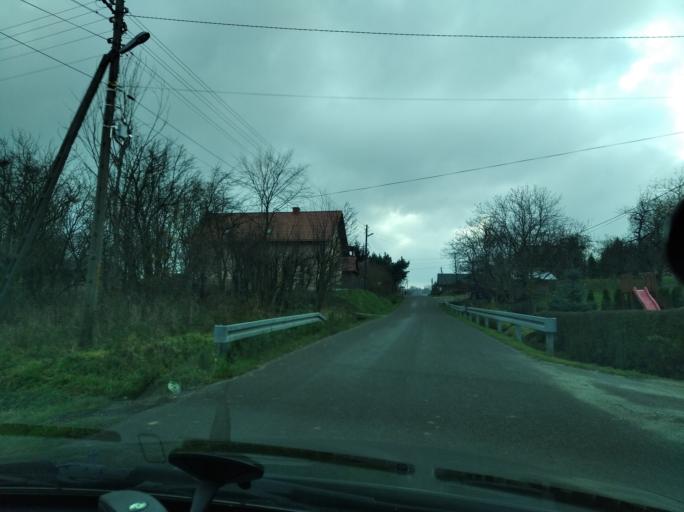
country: PL
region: Subcarpathian Voivodeship
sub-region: Powiat przeworski
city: Sietesz
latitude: 49.9845
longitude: 22.3459
